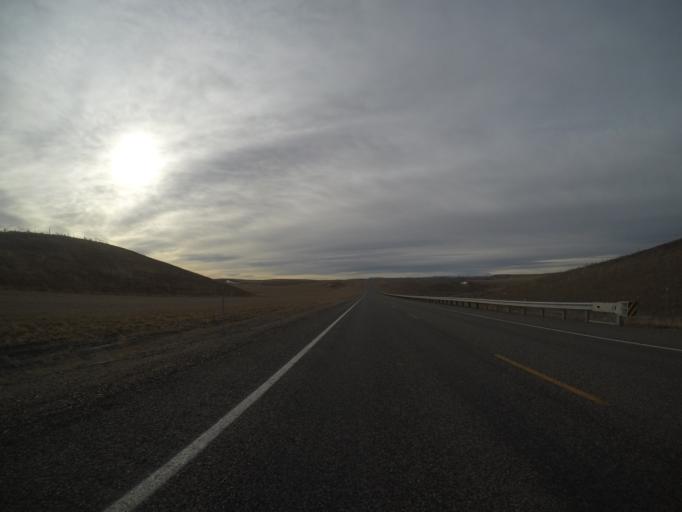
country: US
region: Montana
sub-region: Yellowstone County
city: Laurel
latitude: 45.5727
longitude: -108.8473
